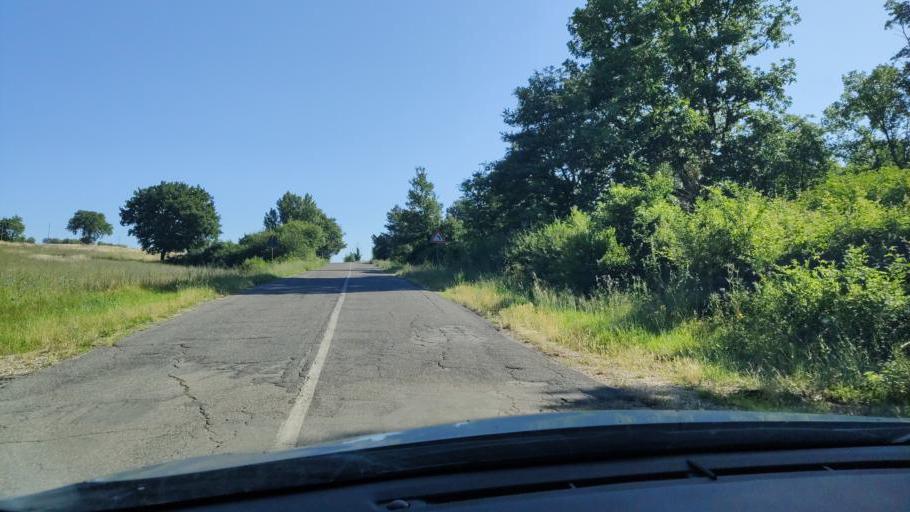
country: IT
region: Umbria
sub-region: Provincia di Terni
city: Avigliano Umbro
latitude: 42.6413
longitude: 12.4182
